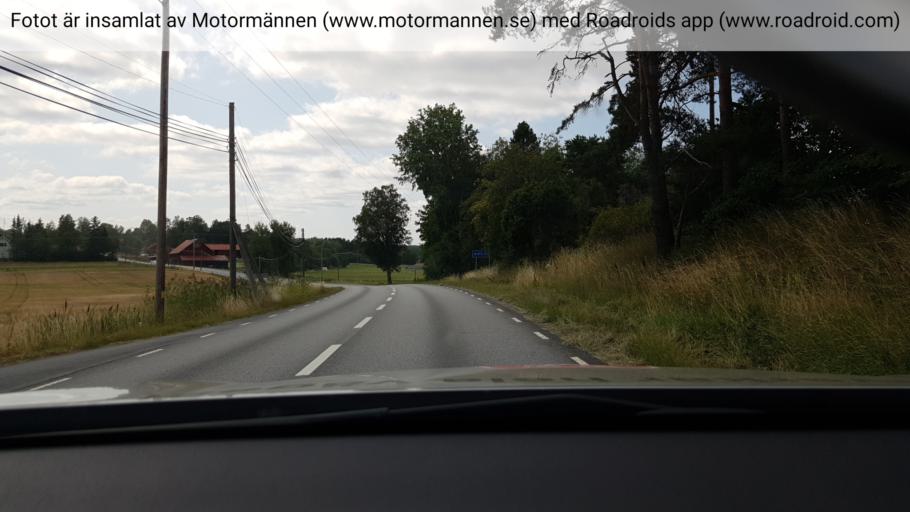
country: SE
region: Stockholm
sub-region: Vallentuna Kommun
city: Vallentuna
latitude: 59.5418
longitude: 18.1713
